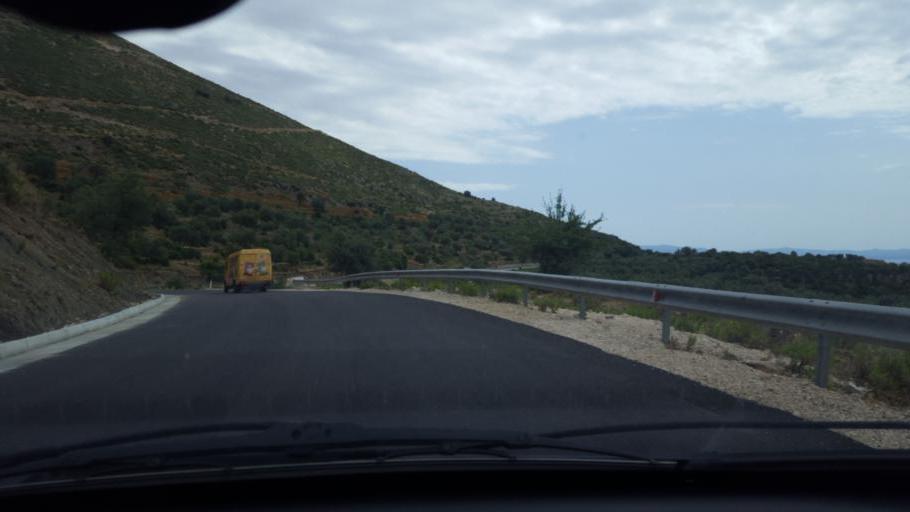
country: AL
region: Vlore
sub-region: Rrethi i Sarandes
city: Lukove
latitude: 40.0327
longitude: 19.8869
